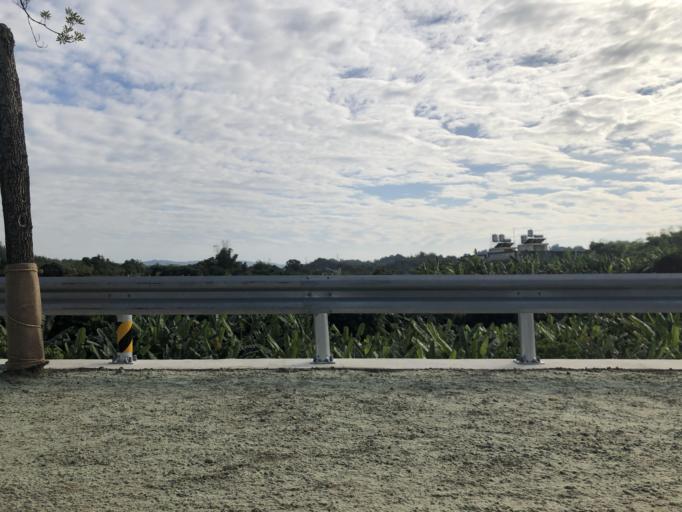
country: TW
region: Taiwan
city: Yujing
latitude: 23.0531
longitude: 120.4076
